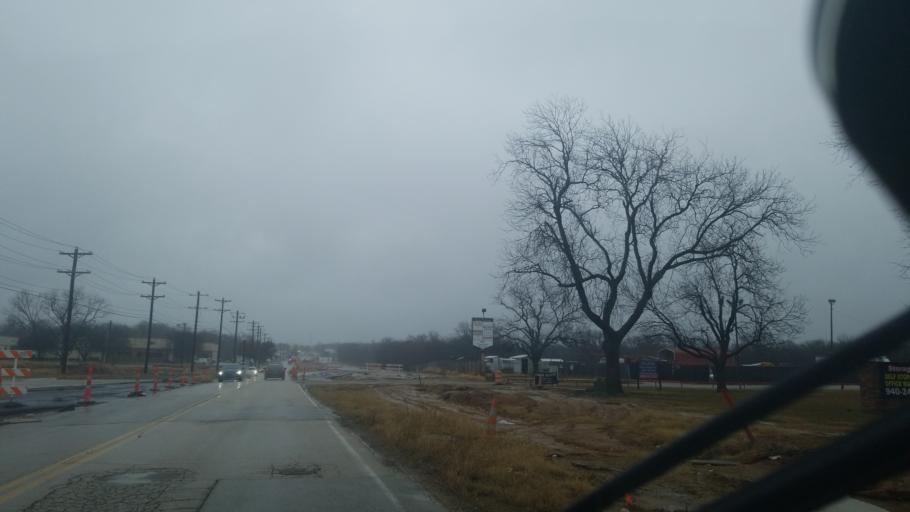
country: US
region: Texas
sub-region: Denton County
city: Denton
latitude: 33.2028
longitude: -97.0844
